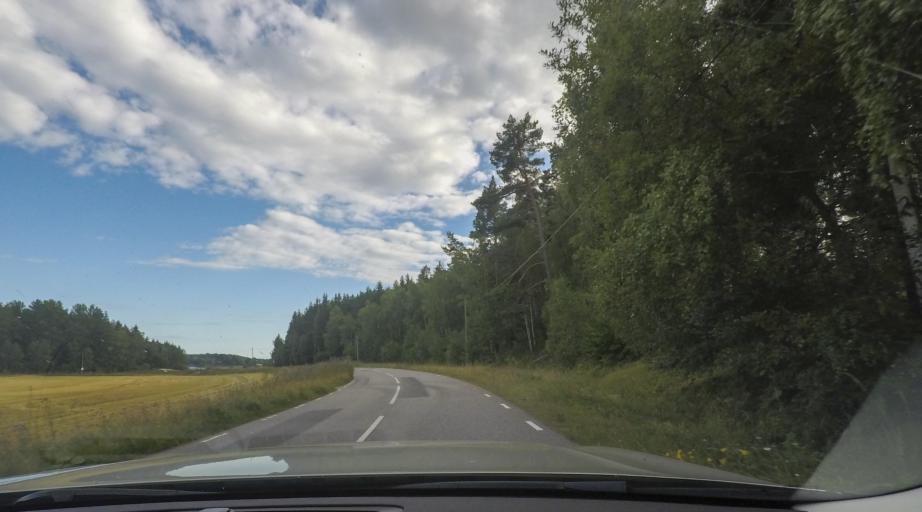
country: SE
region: Soedermanland
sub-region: Trosa Kommun
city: Trosa
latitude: 58.9745
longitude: 17.6932
